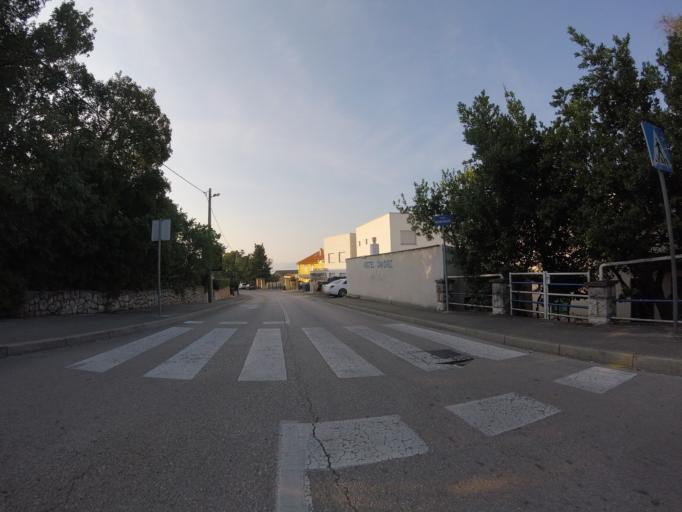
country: HR
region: Primorsko-Goranska
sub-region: Grad Crikvenica
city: Crikvenica
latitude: 45.1927
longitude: 14.6681
